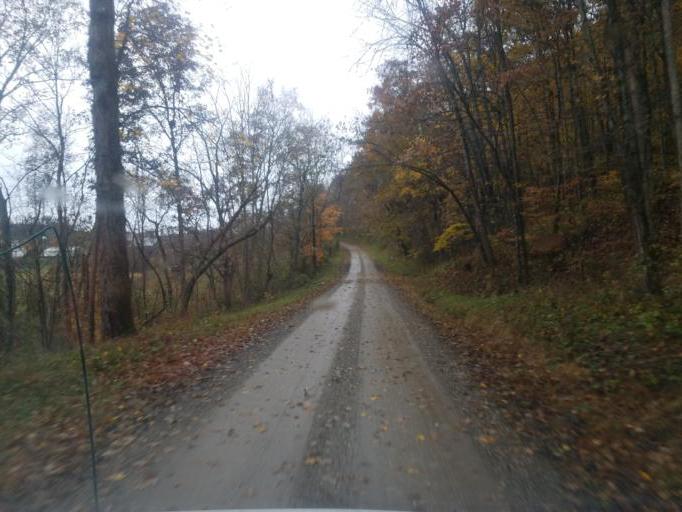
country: US
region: Ohio
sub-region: Washington County
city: Beverly
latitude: 39.4597
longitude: -81.7786
